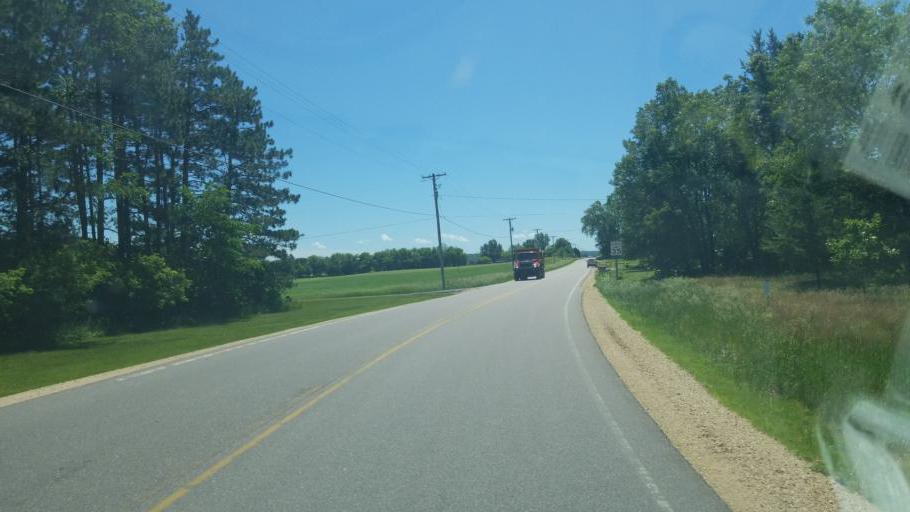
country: US
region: Wisconsin
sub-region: Juneau County
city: New Lisbon
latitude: 43.9133
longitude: -90.2619
